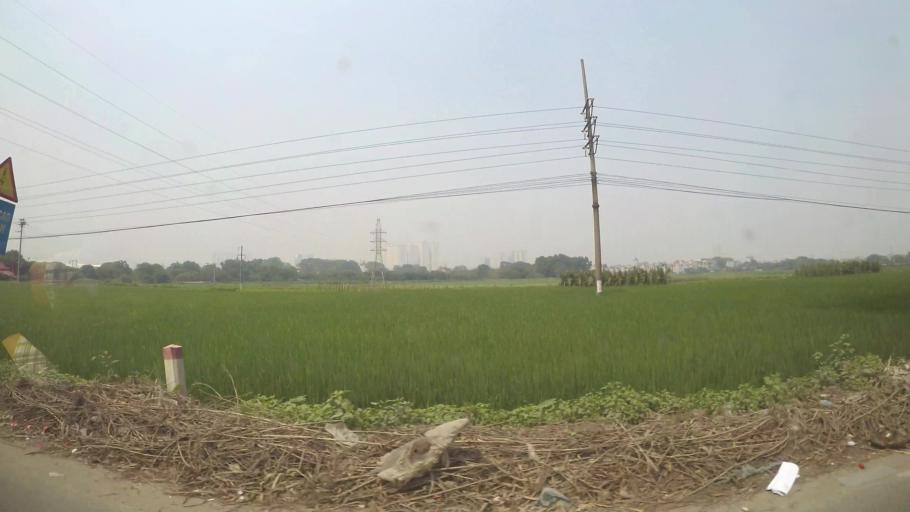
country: VN
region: Ha Noi
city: Van Dien
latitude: 20.9502
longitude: 105.8211
